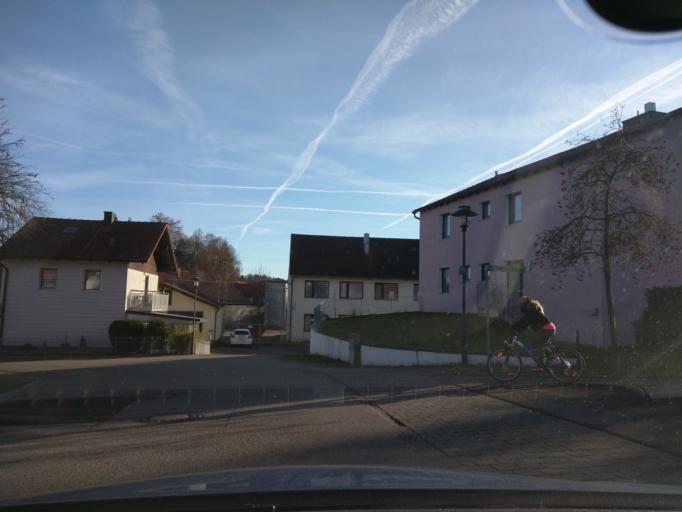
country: DE
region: Bavaria
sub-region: Upper Bavaria
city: Au in der Hallertau
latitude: 48.5549
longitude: 11.7460
